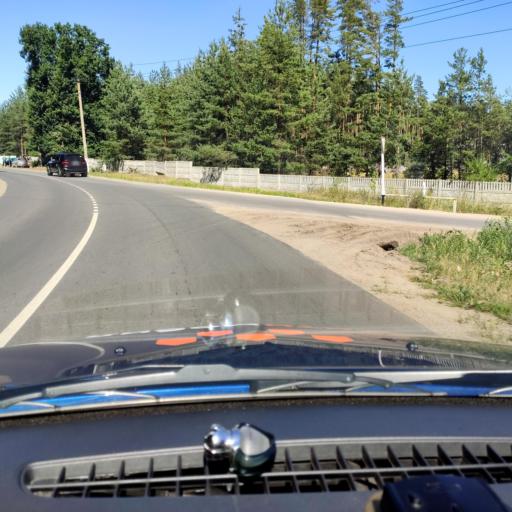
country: RU
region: Voronezj
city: Podgornoye
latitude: 51.7858
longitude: 39.1460
